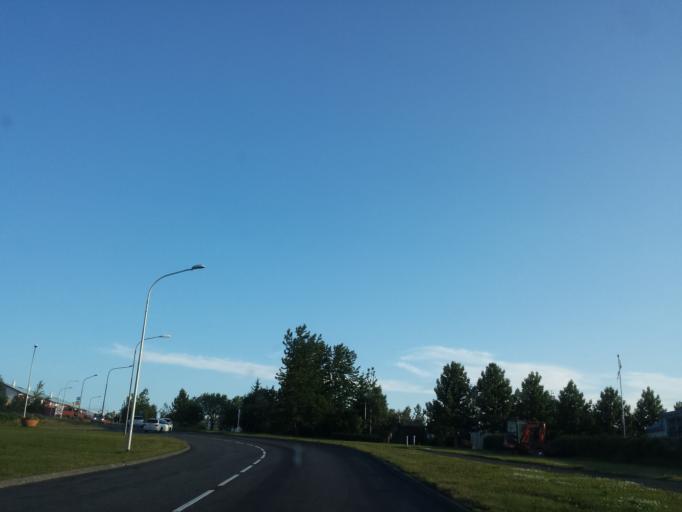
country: IS
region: Capital Region
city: Mosfellsbaer
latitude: 64.1142
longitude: -21.7850
